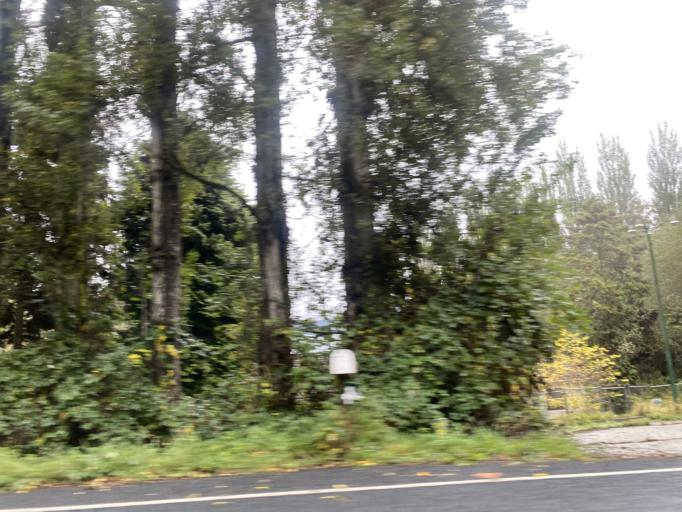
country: US
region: Washington
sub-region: Island County
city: Langley
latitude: 48.0438
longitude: -122.4320
